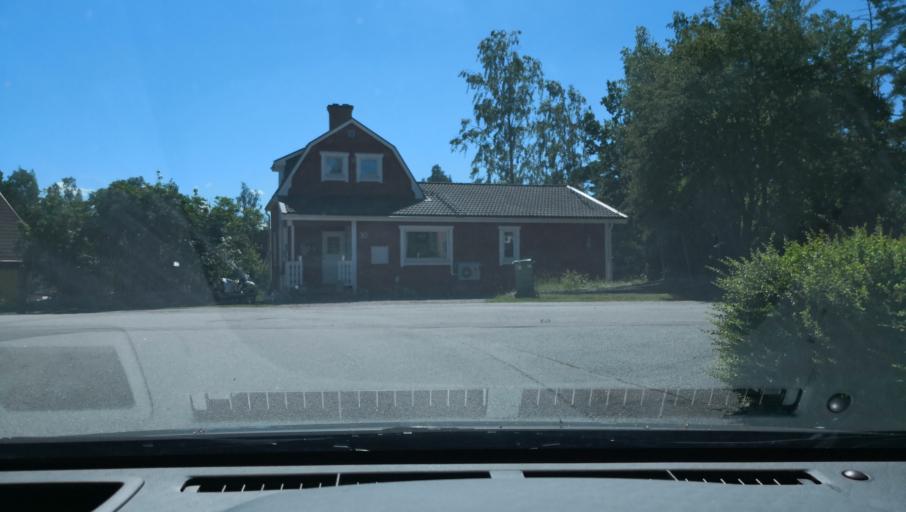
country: SE
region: Vaestmanland
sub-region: Kungsors Kommun
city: Kungsoer
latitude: 59.2793
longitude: 16.1121
